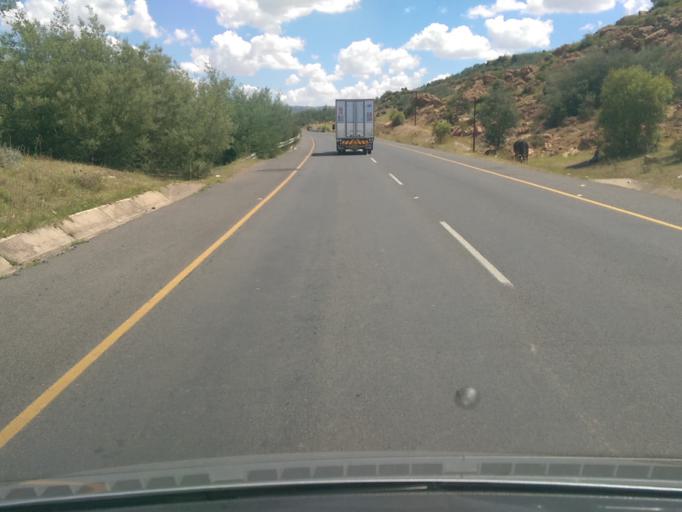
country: LS
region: Maseru
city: Maseru
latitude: -29.3957
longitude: 27.5383
